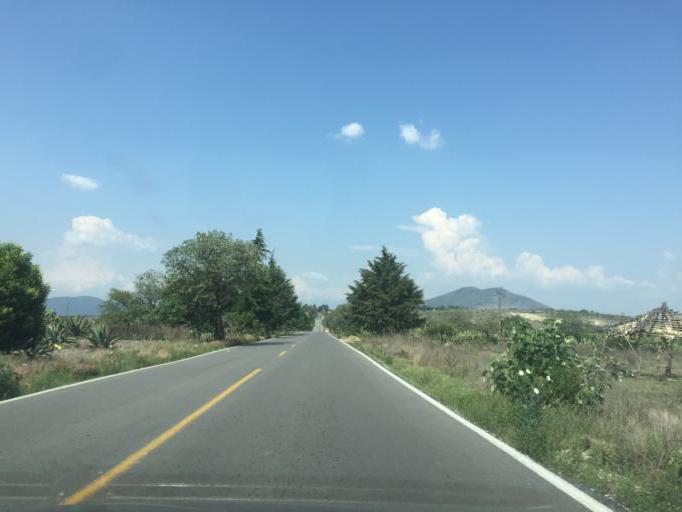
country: MX
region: Hidalgo
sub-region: Cardonal
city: Pozuelos
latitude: 20.6148
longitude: -99.0543
